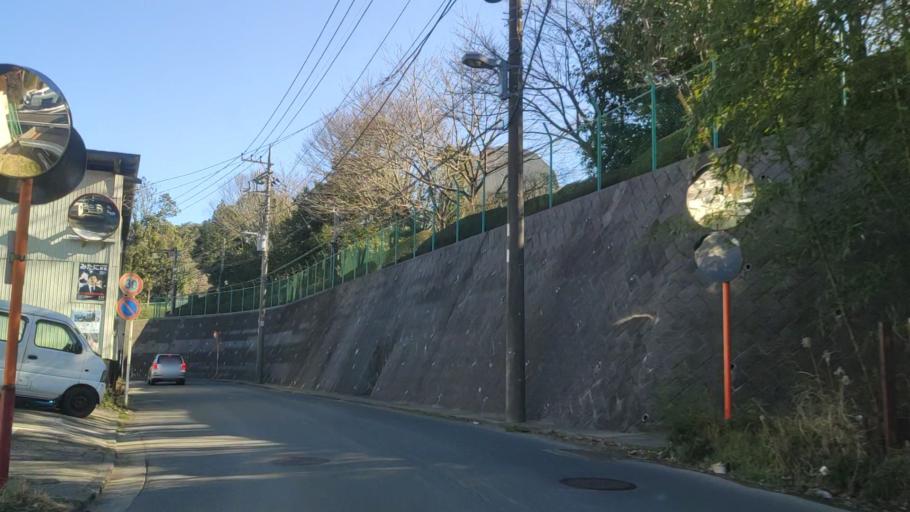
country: JP
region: Kanagawa
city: Minami-rinkan
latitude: 35.5064
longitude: 139.5136
